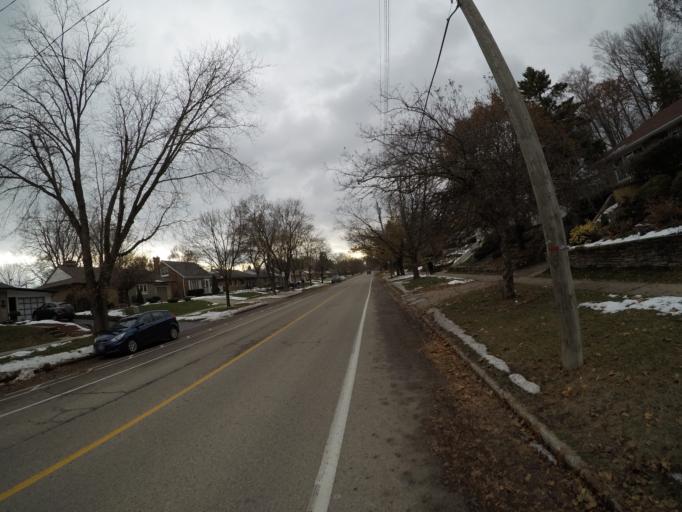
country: CA
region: Ontario
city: Waterloo
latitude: 43.4704
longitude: -80.4913
